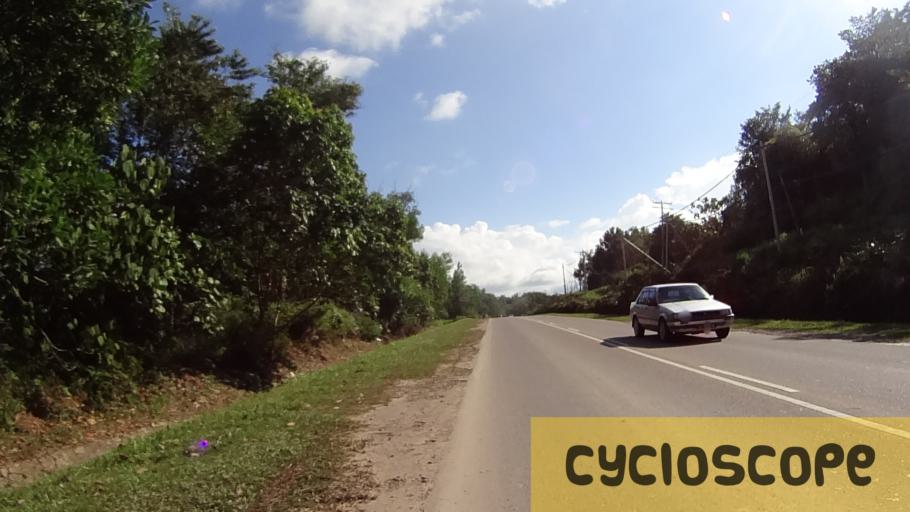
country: MY
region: Sabah
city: Beaufort
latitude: 5.0313
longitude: 115.5440
